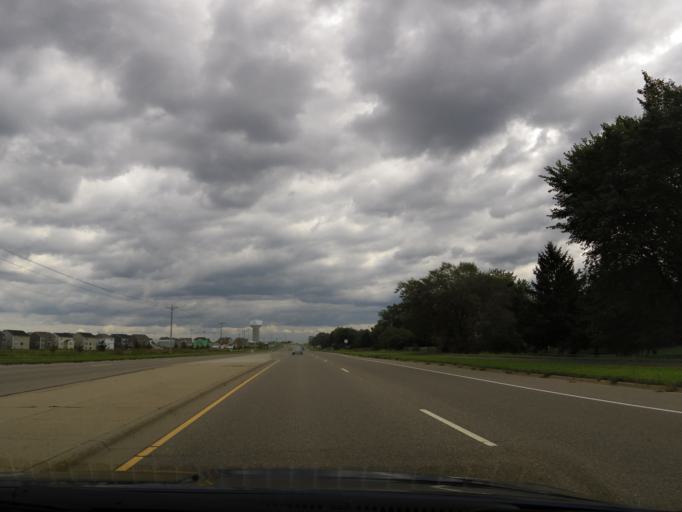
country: US
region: Minnesota
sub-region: Dakota County
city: Apple Valley
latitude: 44.7173
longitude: -93.1907
